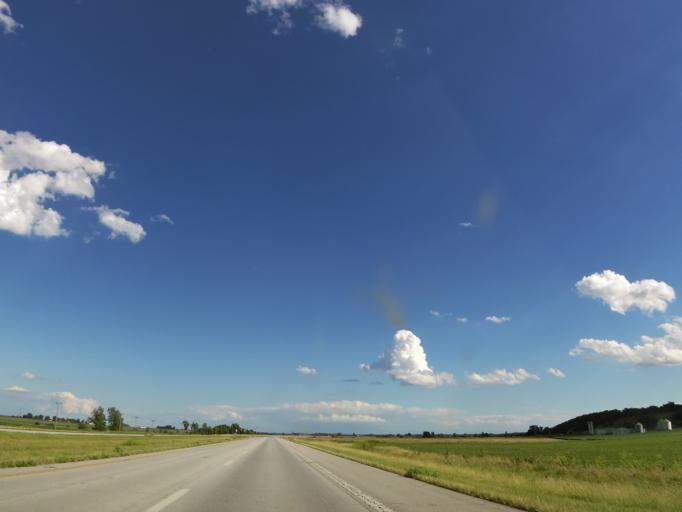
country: US
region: Illinois
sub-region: Adams County
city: Quincy
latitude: 39.9743
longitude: -91.5214
